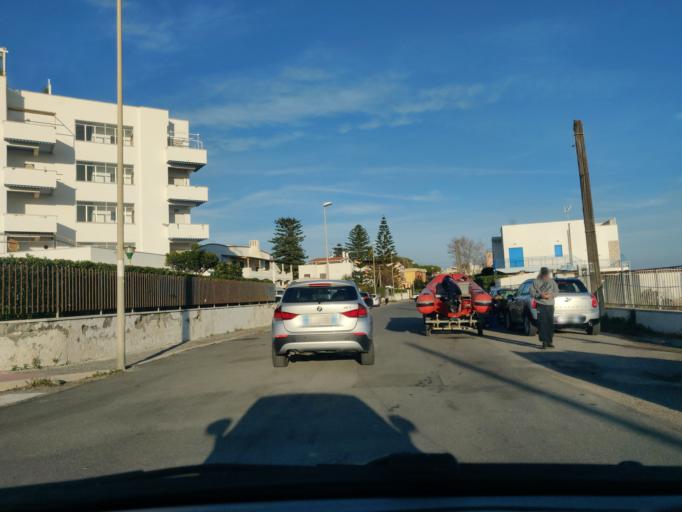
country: IT
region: Latium
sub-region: Citta metropolitana di Roma Capitale
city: Santa Marinella
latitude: 42.0304
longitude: 11.8415
